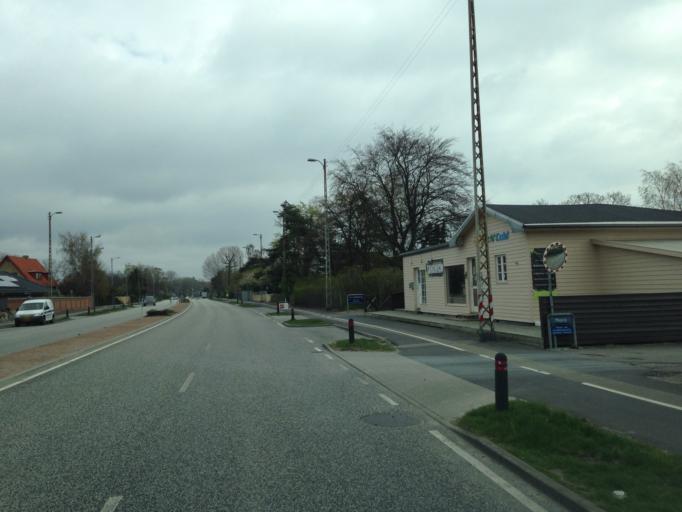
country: DK
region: Capital Region
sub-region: Ishoj Kommune
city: Ishoj
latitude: 55.5905
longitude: 12.3357
